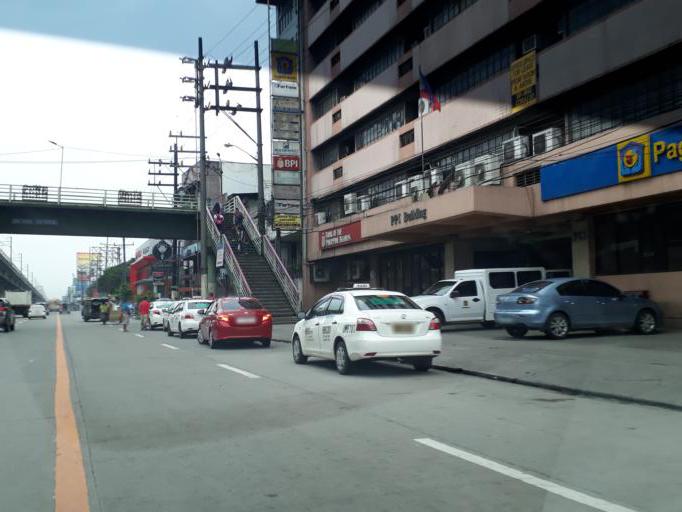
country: PH
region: Calabarzon
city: Del Monte
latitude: 14.6575
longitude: 120.9972
